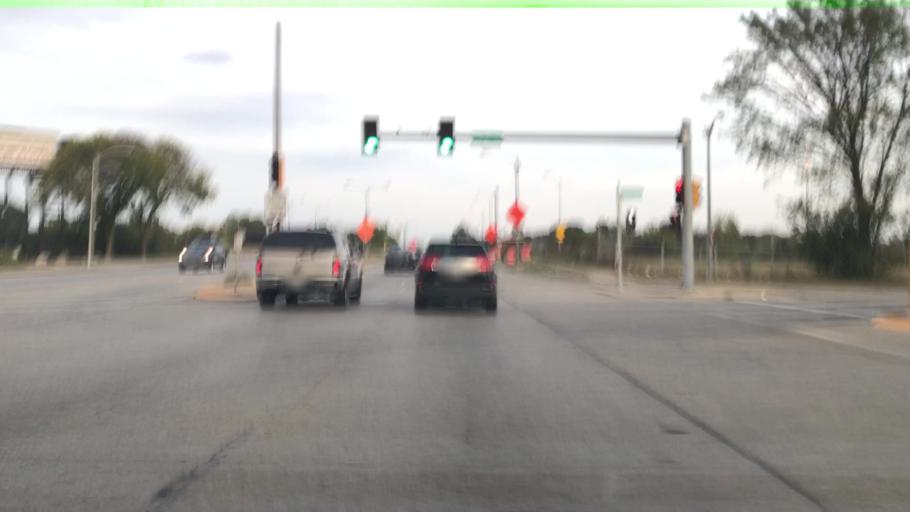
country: US
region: Wisconsin
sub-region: Waukesha County
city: Butler
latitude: 43.1195
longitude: -88.0141
